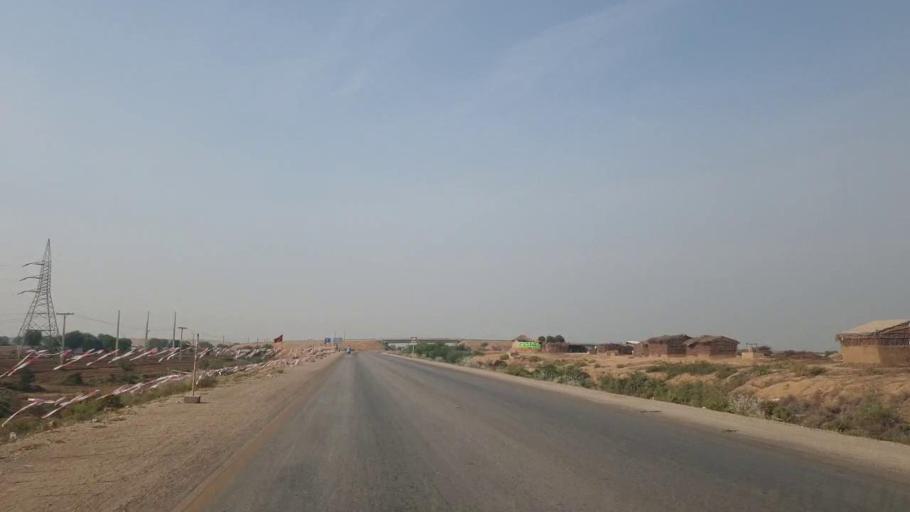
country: PK
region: Sindh
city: Sann
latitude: 26.1523
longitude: 68.0265
